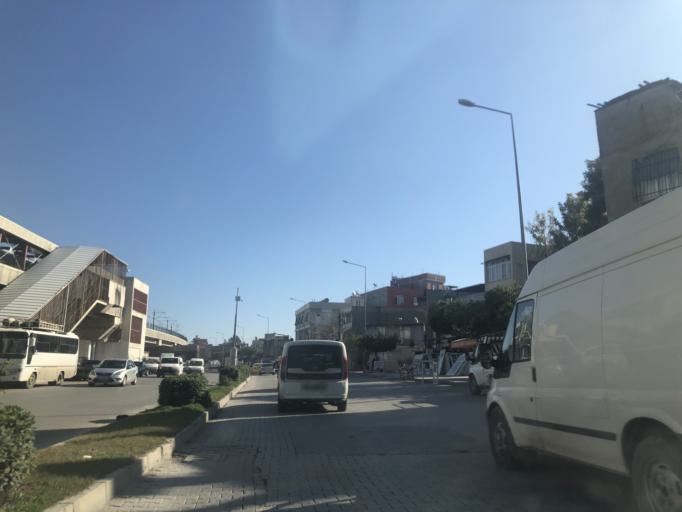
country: TR
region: Adana
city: Seyhan
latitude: 36.9787
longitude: 35.3253
